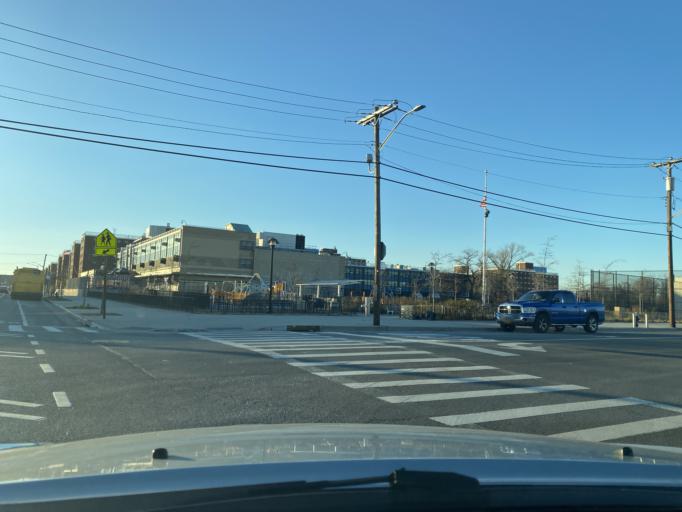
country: US
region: New York
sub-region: Nassau County
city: Inwood
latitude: 40.5954
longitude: -73.7799
